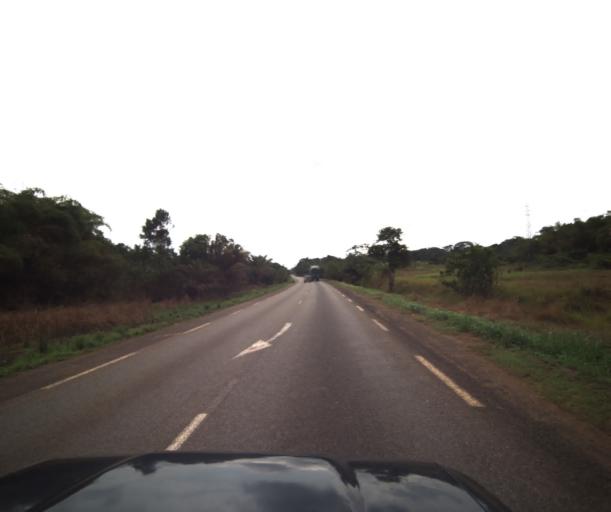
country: CM
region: Littoral
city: Edea
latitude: 3.8352
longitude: 10.4321
